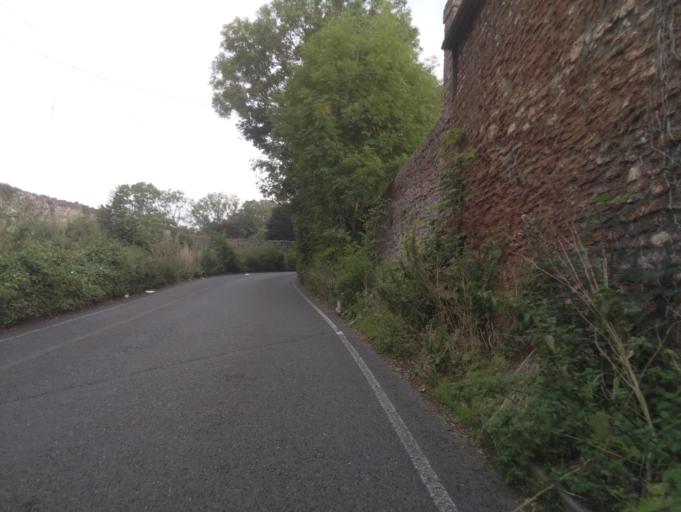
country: GB
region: England
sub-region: North Somerset
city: Nailsea
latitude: 51.4450
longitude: -2.7335
